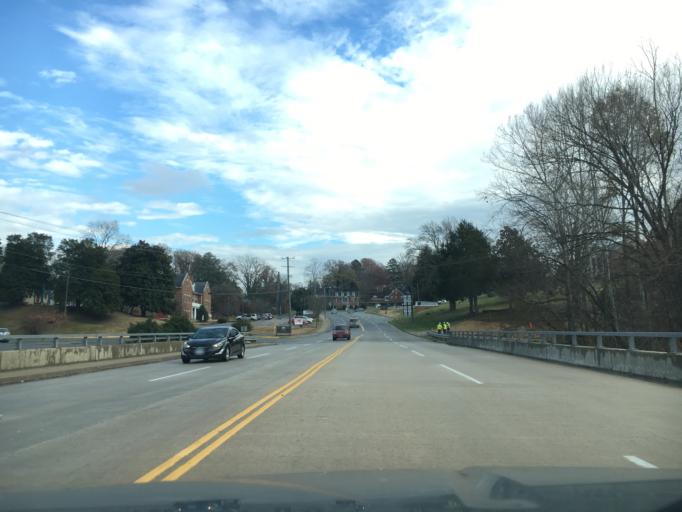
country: US
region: Virginia
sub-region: Prince Edward County
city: Farmville
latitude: 37.3038
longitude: -78.4065
